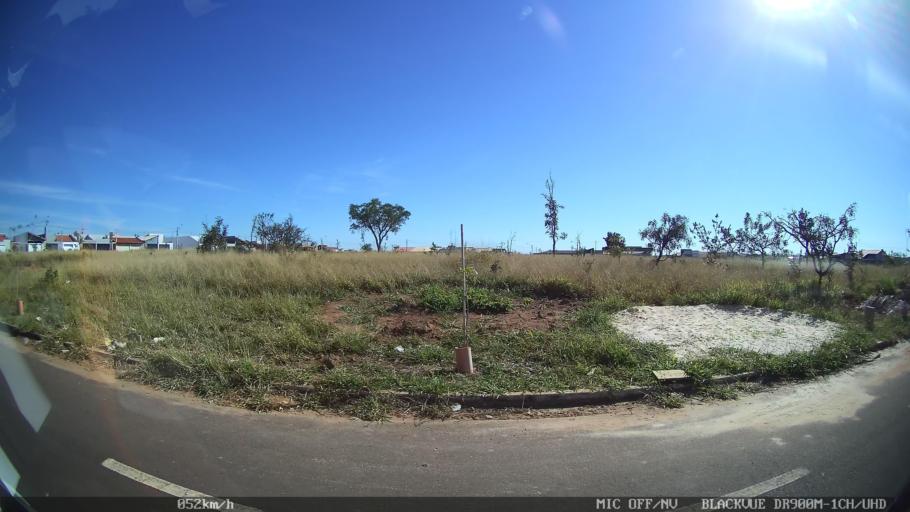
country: BR
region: Sao Paulo
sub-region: Franca
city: Franca
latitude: -20.5681
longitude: -47.3482
